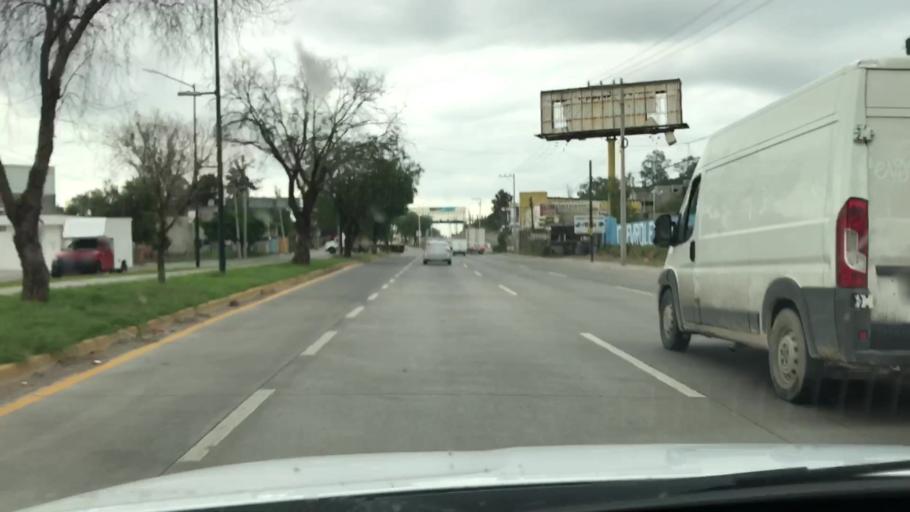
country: MX
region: Guanajuato
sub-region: Leon
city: Malagana (San Antonio del Monte)
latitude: 21.0791
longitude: -101.7506
